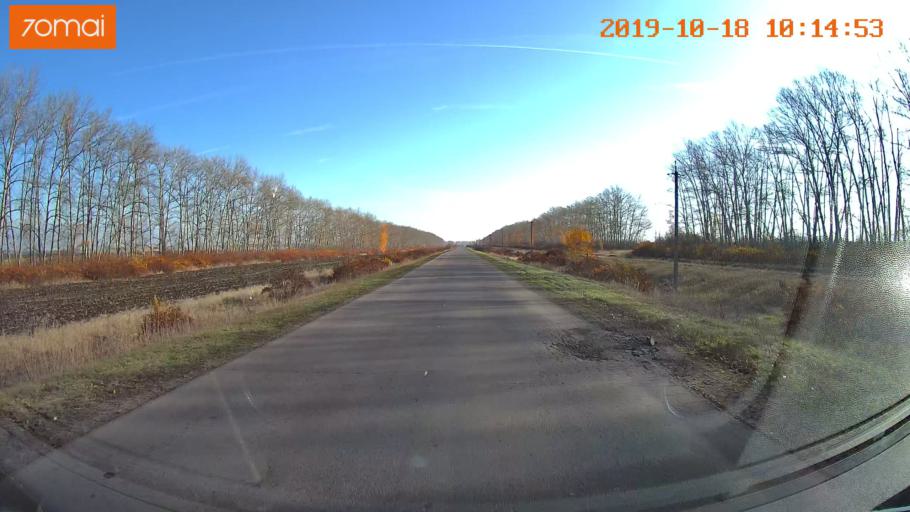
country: RU
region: Tula
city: Kurkino
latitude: 53.4060
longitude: 38.5549
